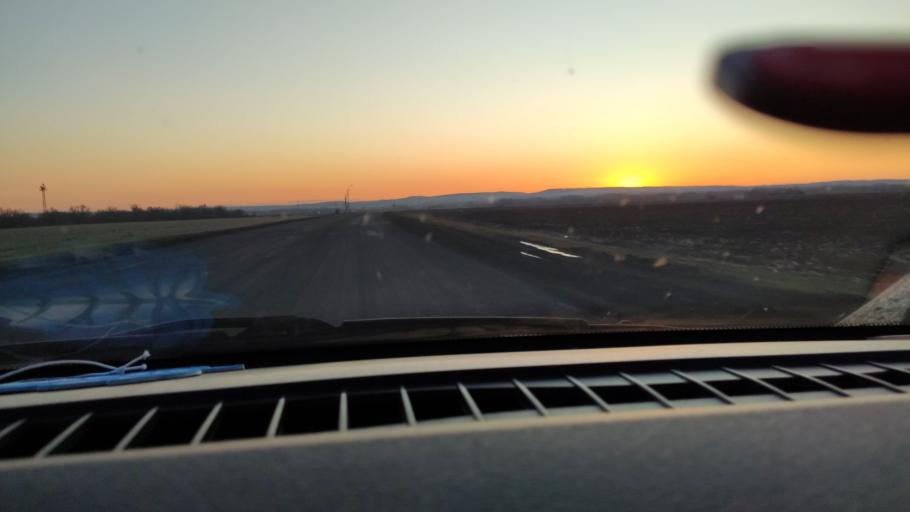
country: RU
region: Saratov
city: Yelshanka
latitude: 51.8109
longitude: 46.2015
